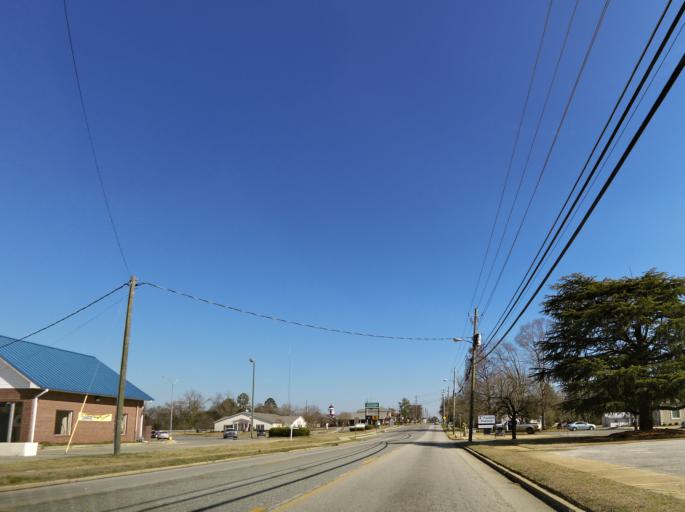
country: US
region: Georgia
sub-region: Bleckley County
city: Cochran
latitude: 32.3834
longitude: -83.3583
